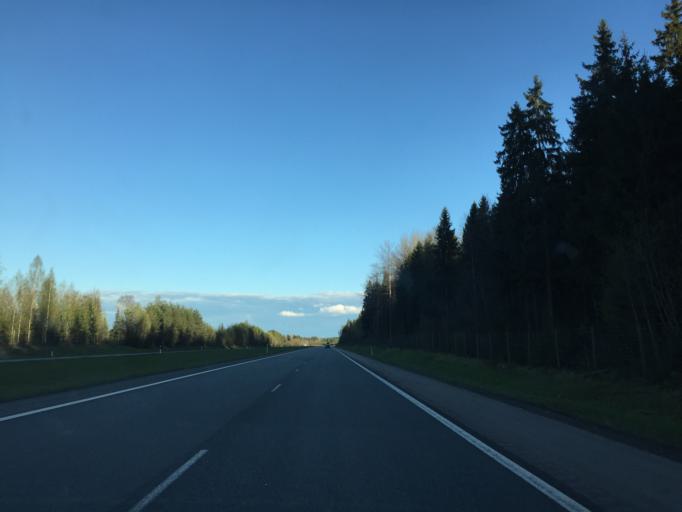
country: FI
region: Haeme
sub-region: Haemeenlinna
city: Tervakoski
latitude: 60.7909
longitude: 24.6955
